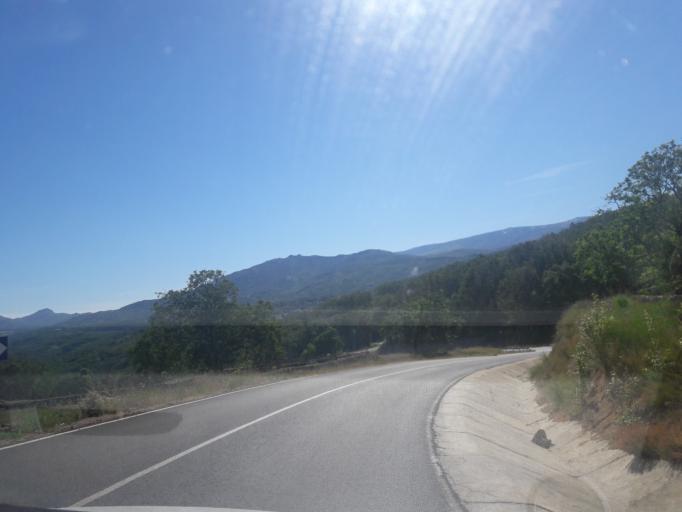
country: ES
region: Castille and Leon
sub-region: Provincia de Salamanca
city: Montemayor del Rio
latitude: 40.3411
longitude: -5.8836
